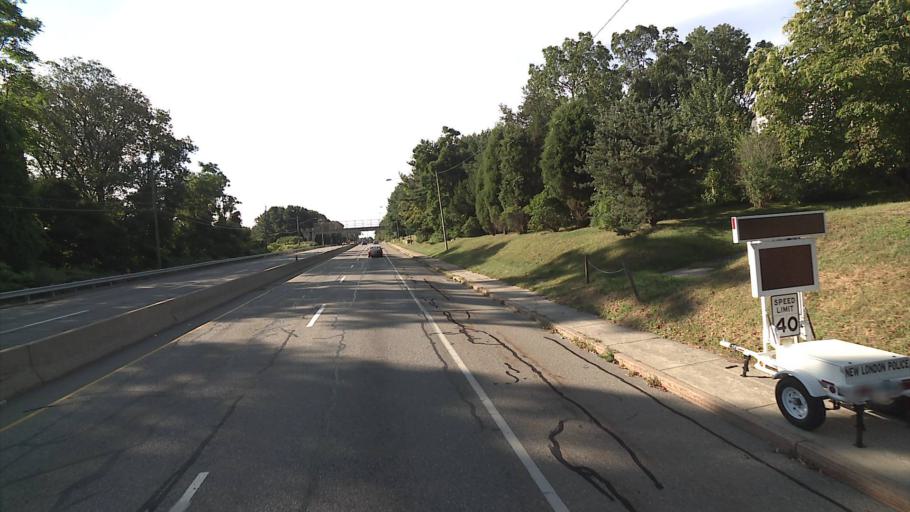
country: US
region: Connecticut
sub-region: New London County
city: New London
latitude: 41.3827
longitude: -72.1051
